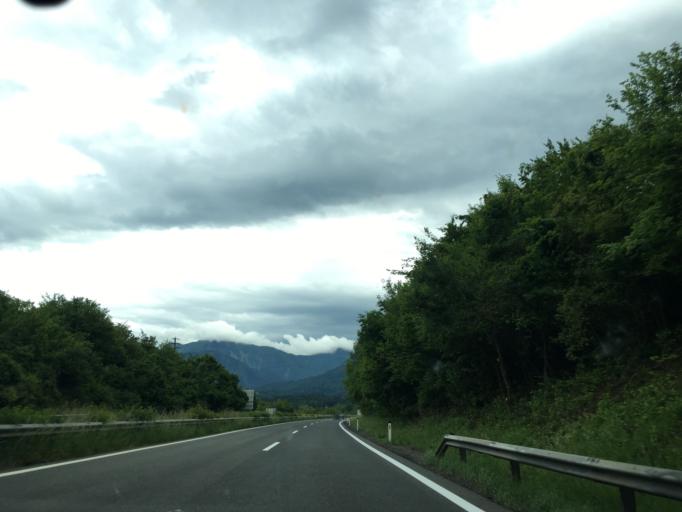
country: AT
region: Carinthia
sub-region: Politischer Bezirk Villach Land
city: Rosegg
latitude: 46.5704
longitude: 14.0058
